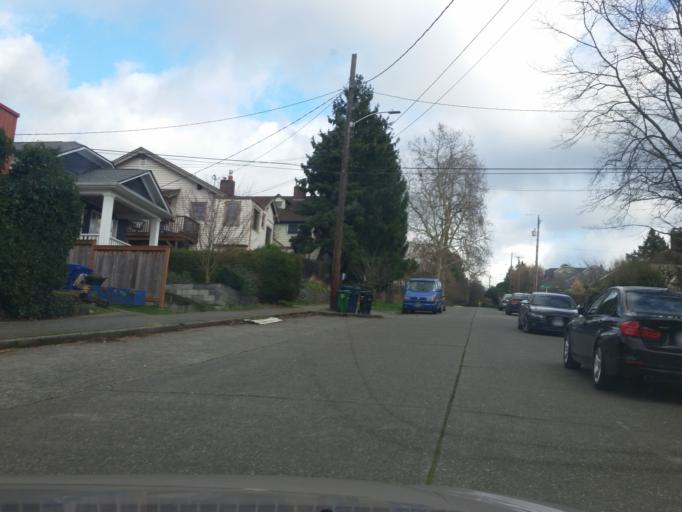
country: US
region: Washington
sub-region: King County
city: Seattle
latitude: 47.6602
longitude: -122.3606
